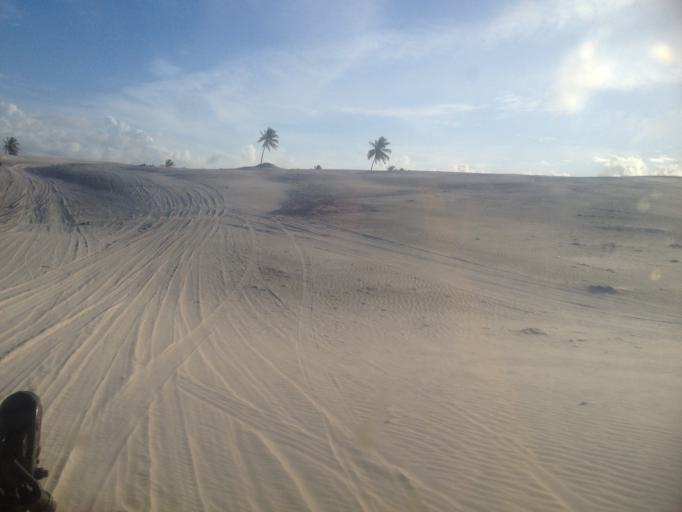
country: BR
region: Sergipe
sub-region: Indiaroba
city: Indiaroba
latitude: -11.4668
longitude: -37.3658
